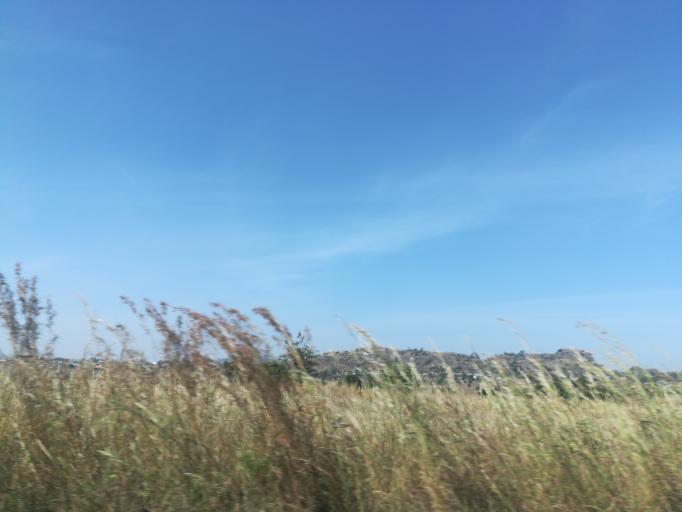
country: NG
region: Plateau
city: Bukuru
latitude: 9.7523
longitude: 8.9077
